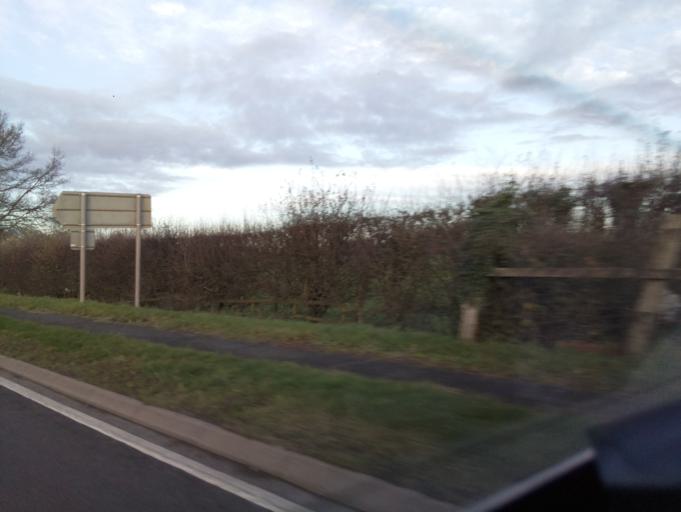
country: GB
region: England
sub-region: Staffordshire
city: Stafford
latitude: 52.8472
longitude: -2.1388
